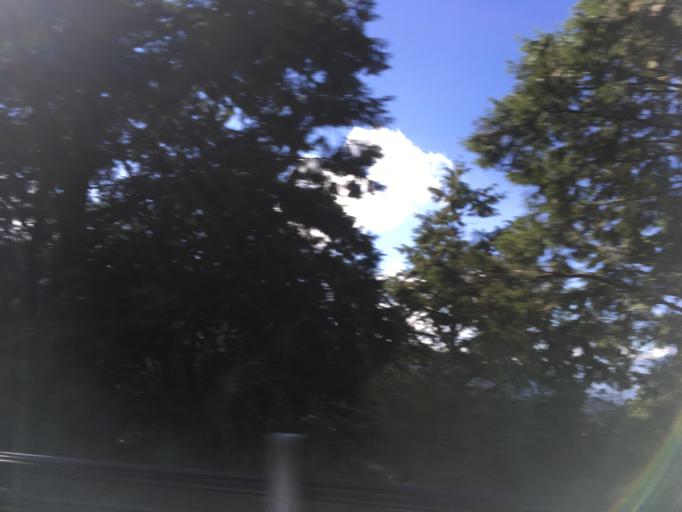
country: TW
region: Taiwan
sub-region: Yilan
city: Yilan
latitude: 24.5151
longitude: 121.5706
